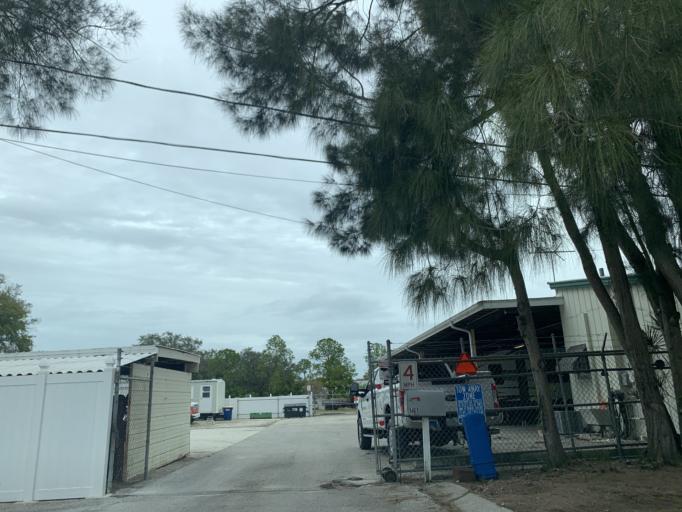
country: US
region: Florida
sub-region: Pinellas County
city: Belleair
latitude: 27.9436
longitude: -82.7883
